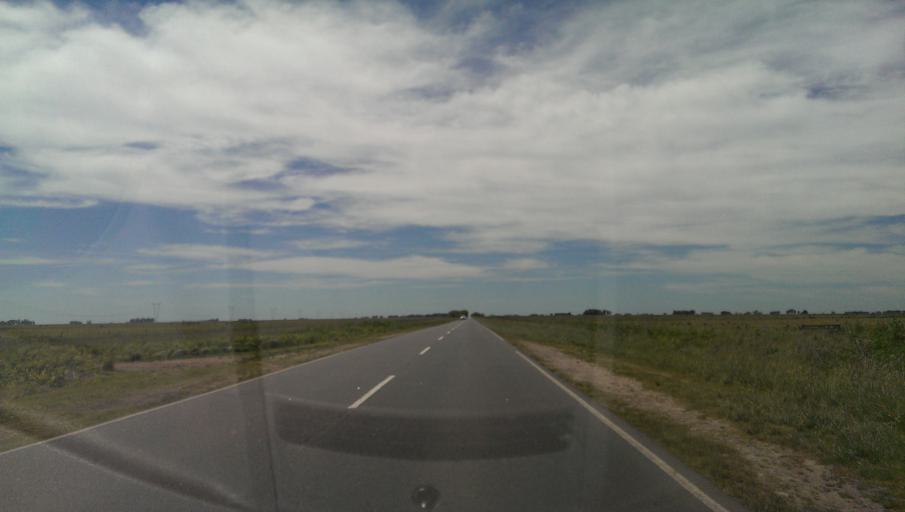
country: AR
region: Buenos Aires
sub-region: Partido de Laprida
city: Laprida
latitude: -37.2249
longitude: -60.7013
